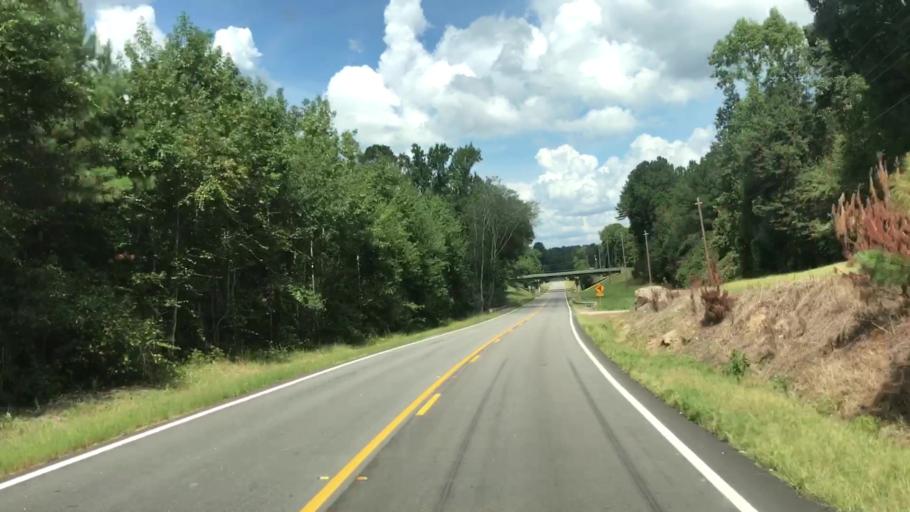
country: US
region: Georgia
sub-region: Greene County
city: Union Point
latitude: 33.5430
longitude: -83.0946
